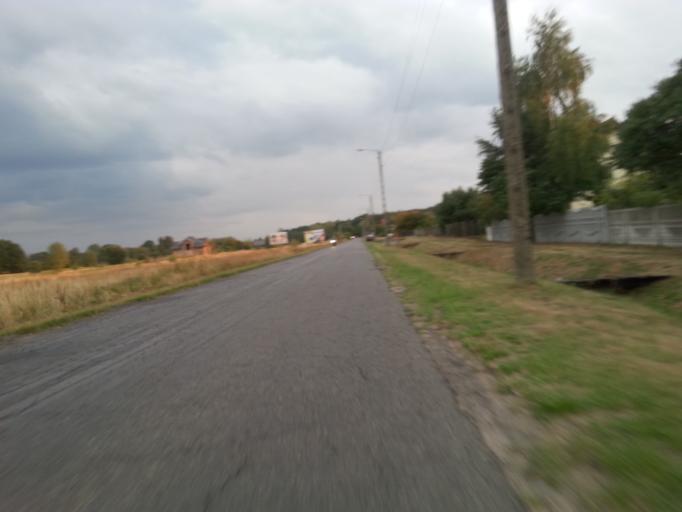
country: PL
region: Lower Silesian Voivodeship
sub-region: Powiat olesnicki
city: Twardogora
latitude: 51.3552
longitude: 17.4540
